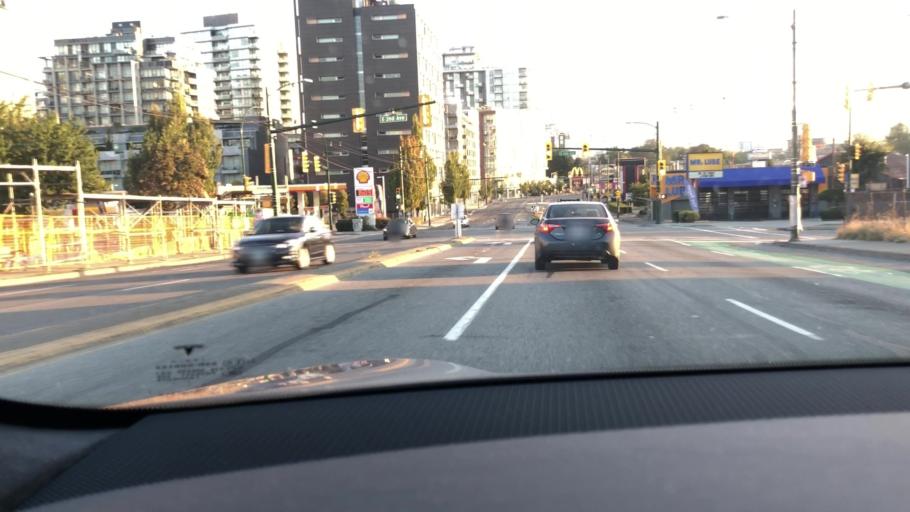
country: CA
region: British Columbia
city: Vancouver
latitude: 49.2685
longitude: -123.1007
